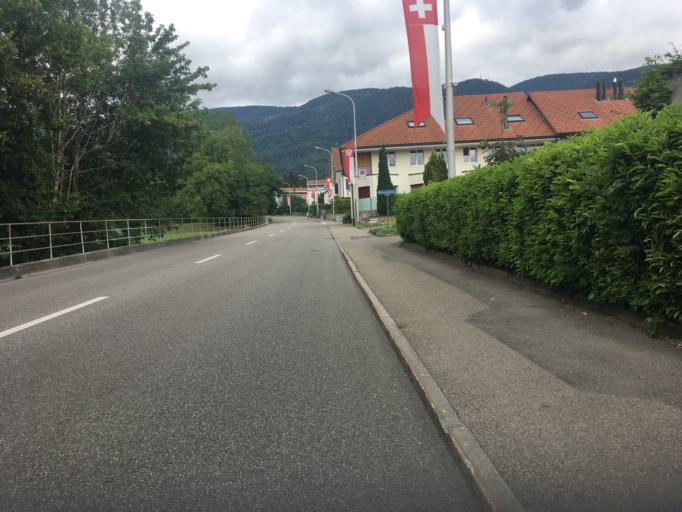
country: CH
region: Solothurn
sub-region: Bezirk Lebern
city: Langendorf
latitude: 47.2231
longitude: 7.5144
